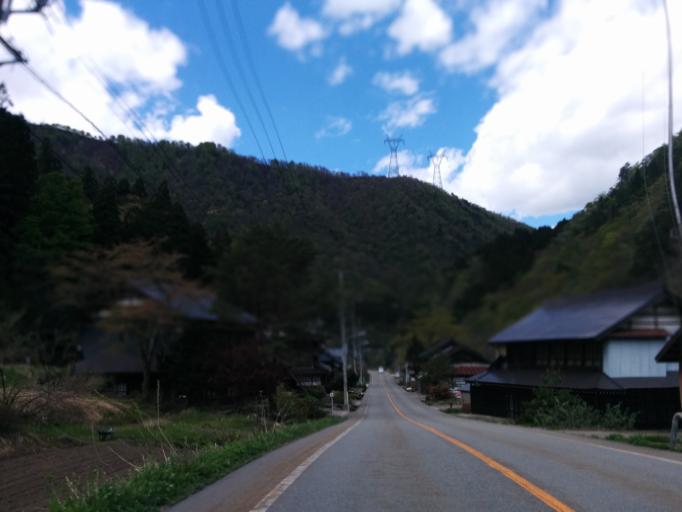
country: JP
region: Toyama
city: Fukumitsu
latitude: 36.3216
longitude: 136.8968
